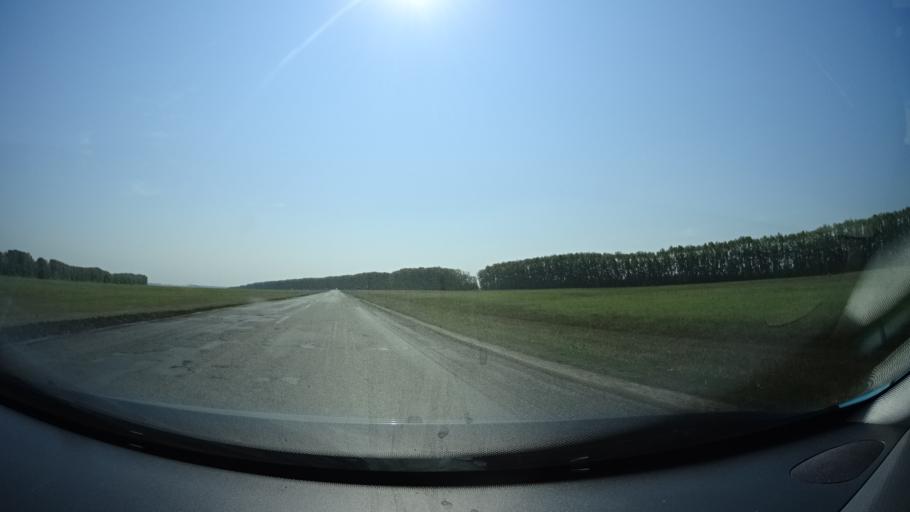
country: RU
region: Bashkortostan
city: Kabakovo
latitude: 54.4559
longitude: 55.9695
